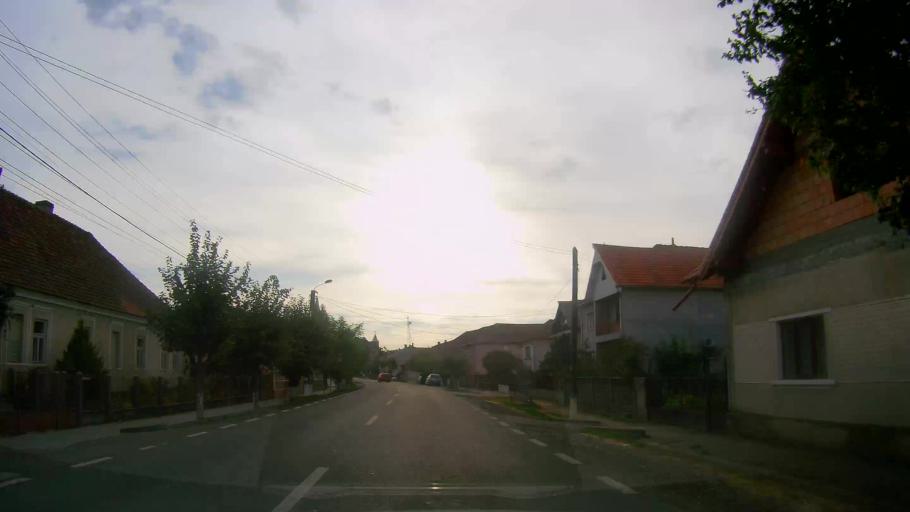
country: RO
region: Satu Mare
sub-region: Comuna Halmeu
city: Halmeu
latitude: 47.9773
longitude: 23.0135
